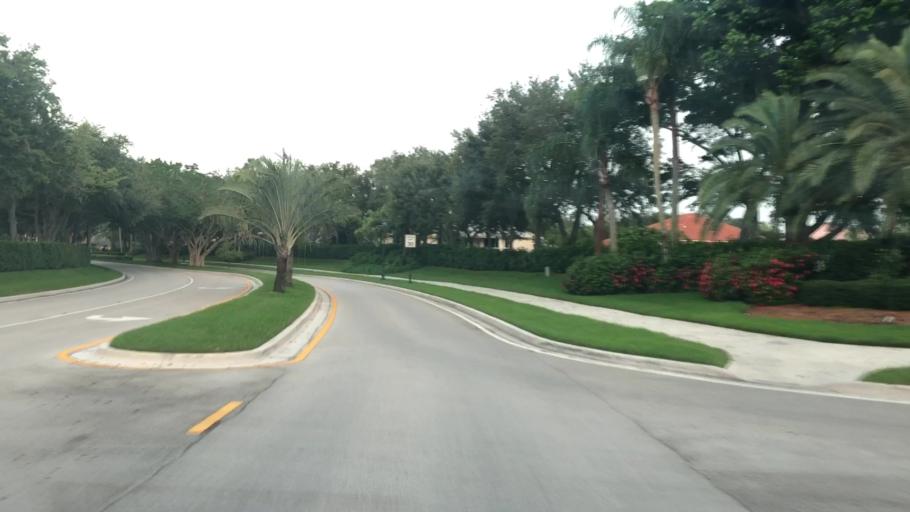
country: US
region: Florida
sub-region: Broward County
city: Weston
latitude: 26.0892
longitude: -80.4000
